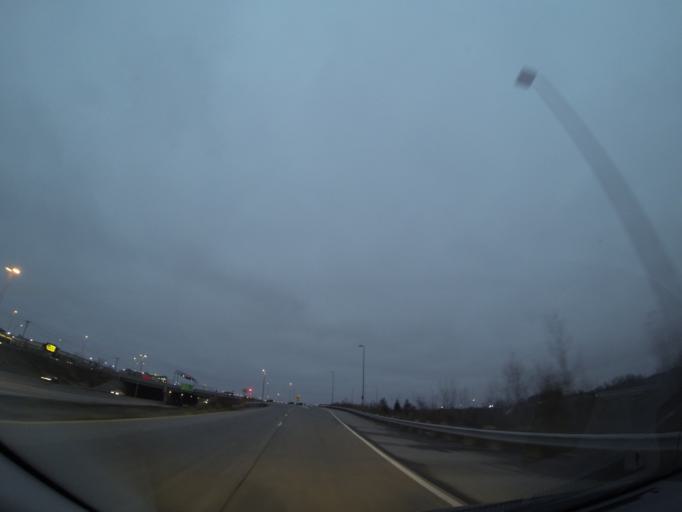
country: US
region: Nebraska
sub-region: Douglas County
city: Elkhorn
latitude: 41.2633
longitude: -96.1775
